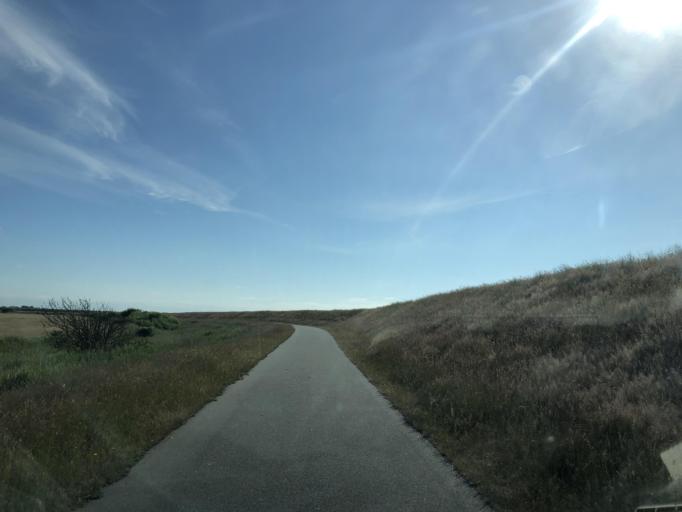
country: DK
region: South Denmark
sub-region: Esbjerg Kommune
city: Tjaereborg
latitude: 55.2920
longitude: 8.5495
